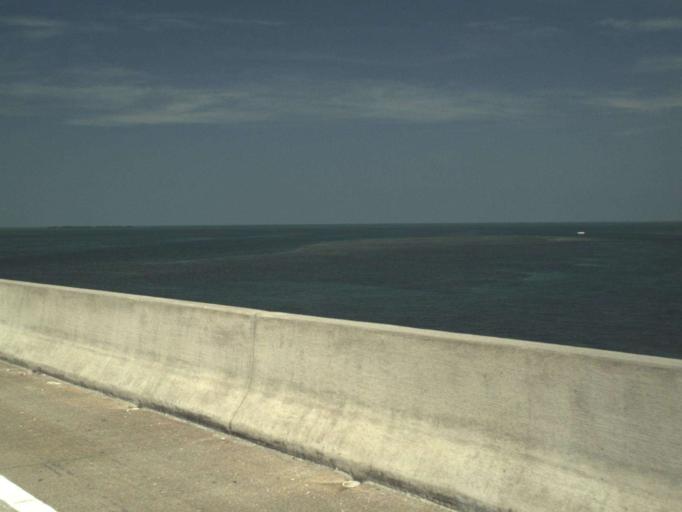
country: US
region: Florida
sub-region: Monroe County
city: Marathon
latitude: 24.7925
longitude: -80.8806
